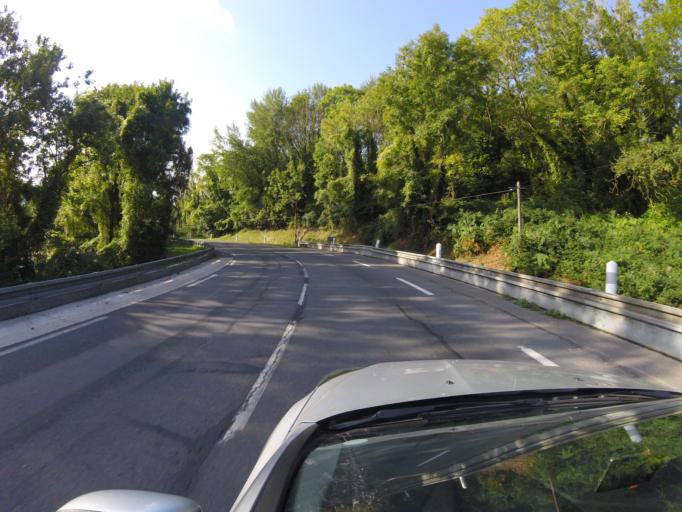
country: FR
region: Haute-Normandie
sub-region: Departement de la Seine-Maritime
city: Fecamp
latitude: 49.7627
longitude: 0.3950
